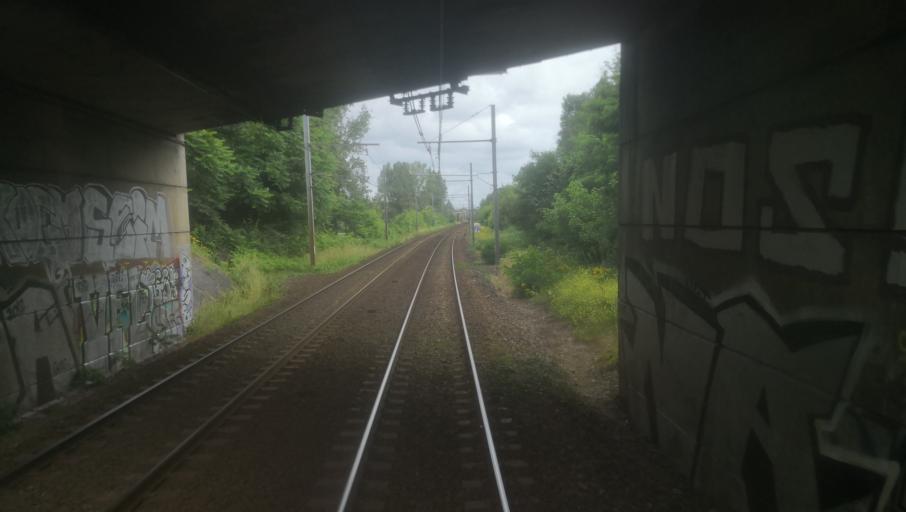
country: FR
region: Aquitaine
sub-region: Departement de la Gironde
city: Villenave-d'Ornon
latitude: 44.7748
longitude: -0.5501
